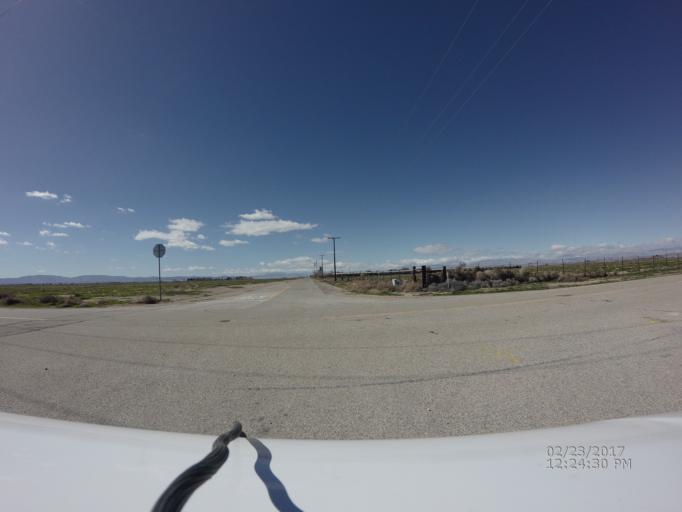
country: US
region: California
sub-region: Los Angeles County
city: Lancaster
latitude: 34.7488
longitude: -118.0054
